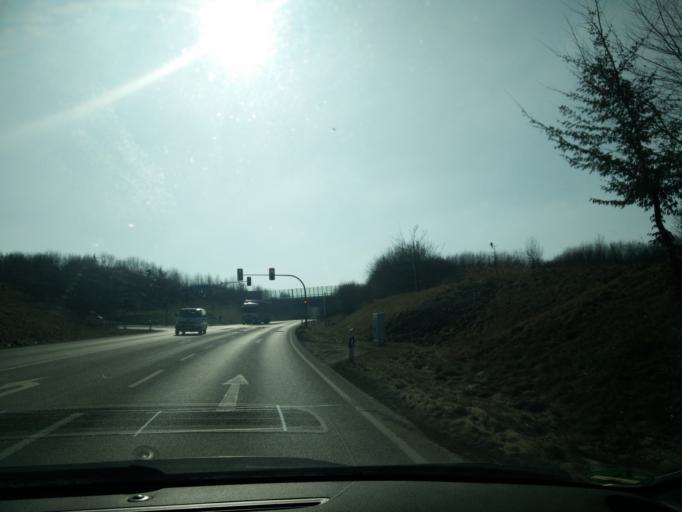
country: DE
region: Saxony
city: Muhlau
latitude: 50.8834
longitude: 12.7832
